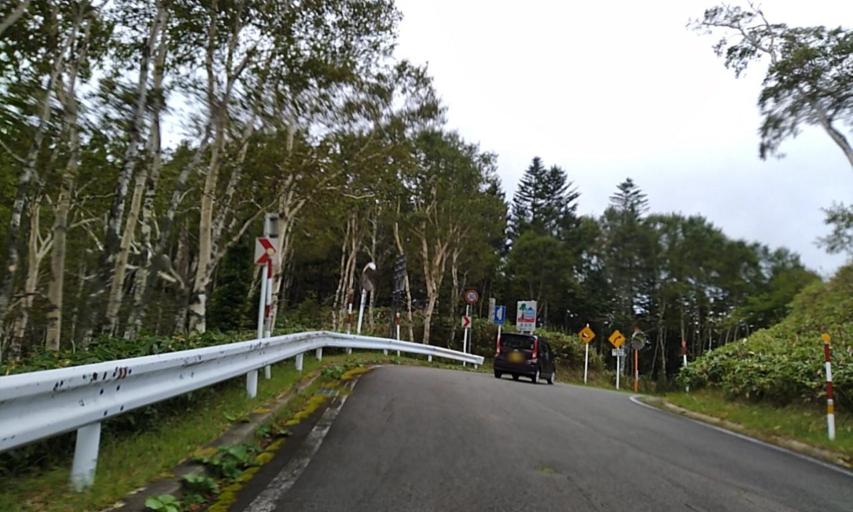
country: JP
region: Hokkaido
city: Bihoro
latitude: 43.5664
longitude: 144.2266
